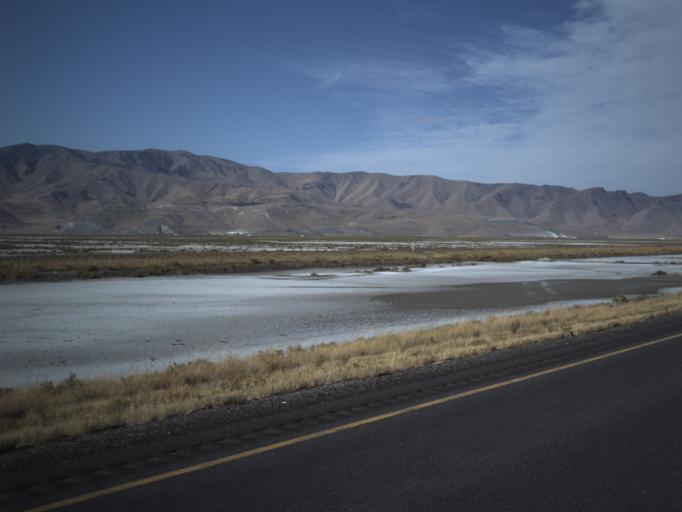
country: US
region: Utah
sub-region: Tooele County
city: Grantsville
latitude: 40.7000
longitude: -112.4855
